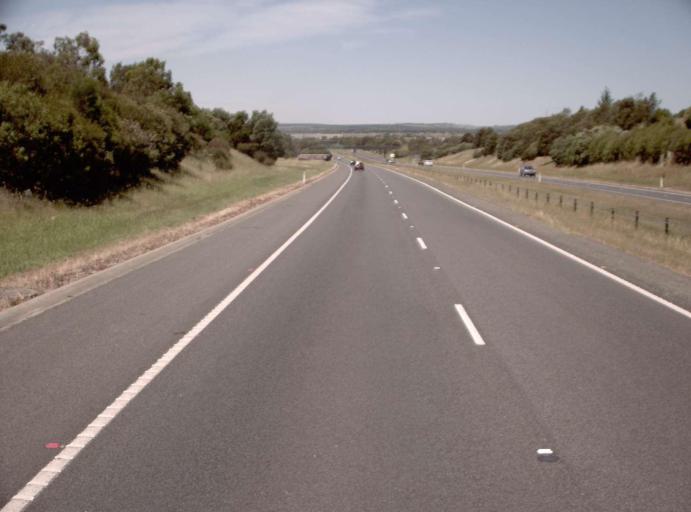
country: AU
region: Victoria
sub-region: Latrobe
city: Morwell
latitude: -38.2420
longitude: 146.4143
